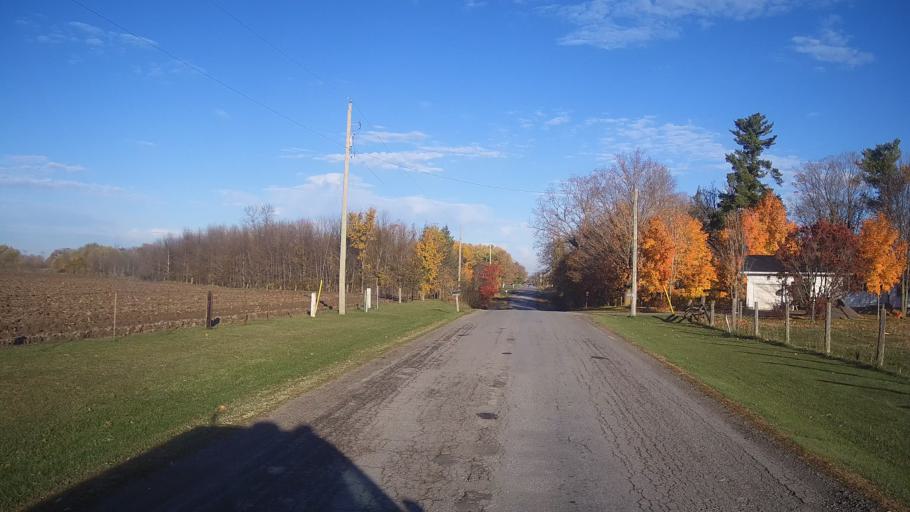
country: CA
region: Ontario
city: Arnprior
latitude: 45.3639
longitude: -76.3162
